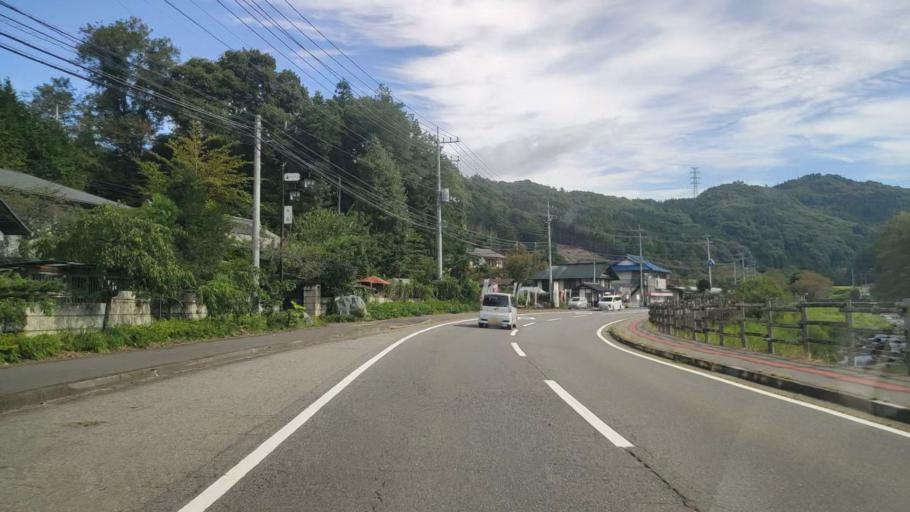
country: JP
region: Gunma
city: Nakanojomachi
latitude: 36.6222
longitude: 138.9168
